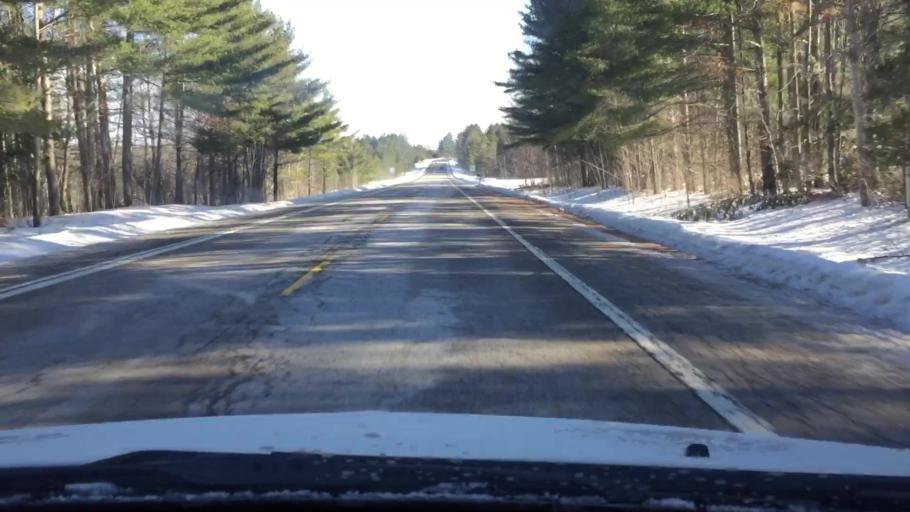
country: US
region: Michigan
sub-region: Charlevoix County
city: East Jordan
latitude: 45.0972
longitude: -85.1064
